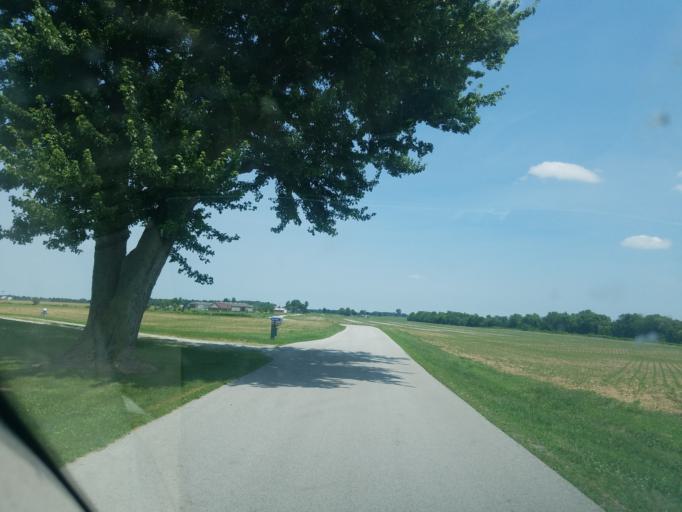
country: US
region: Ohio
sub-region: Wyandot County
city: Carey
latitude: 40.9486
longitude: -83.4974
